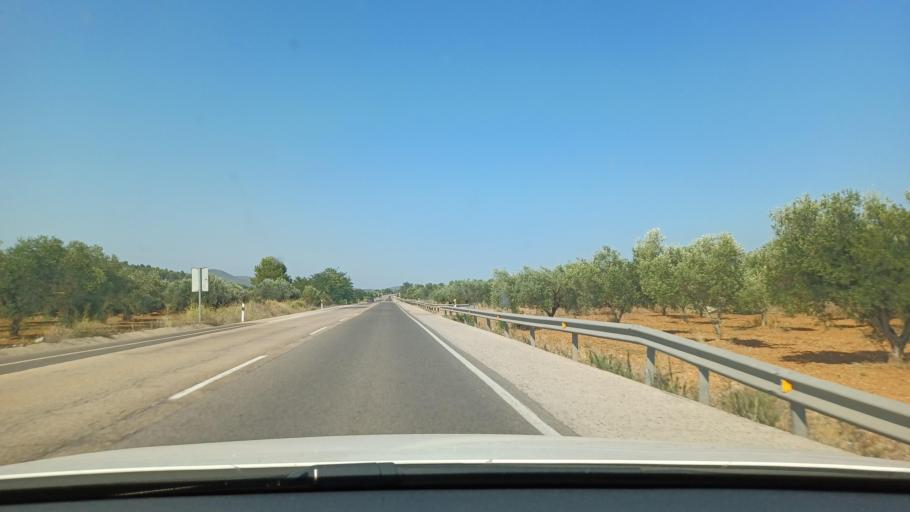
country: ES
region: Valencia
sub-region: Provincia de Castello
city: Santa Magdalena de Pulpis
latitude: 40.3374
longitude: 0.2613
